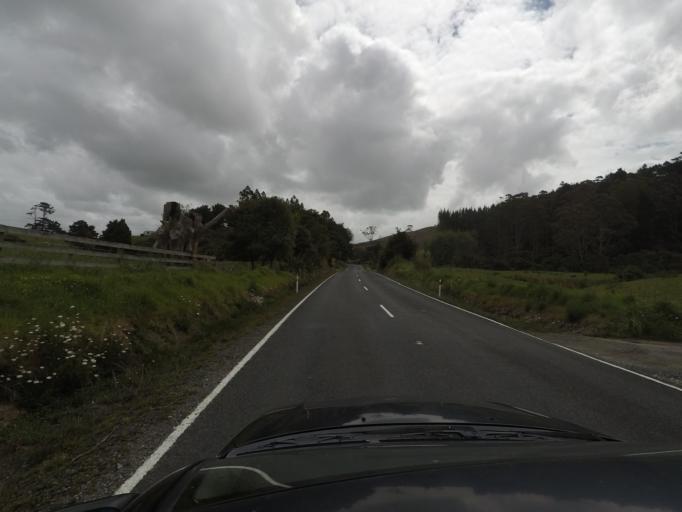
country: NZ
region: Auckland
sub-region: Auckland
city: Parakai
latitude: -36.5024
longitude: 174.4733
